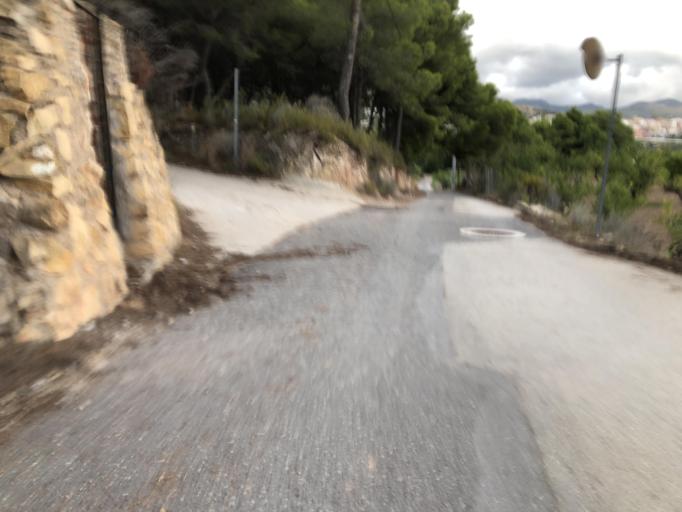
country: ES
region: Valencia
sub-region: Provincia de Alicante
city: Polop
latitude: 38.6390
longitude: -0.1341
